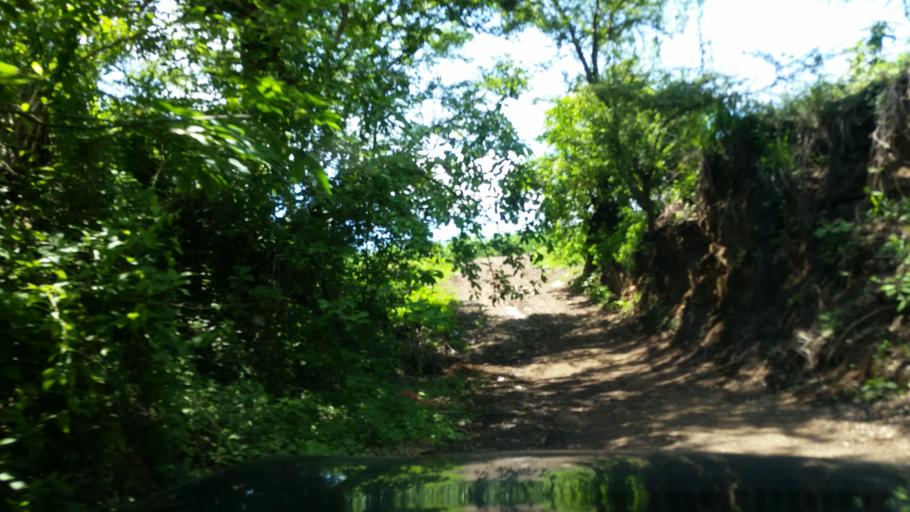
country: NI
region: Chinandega
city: Puerto Morazan
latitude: 12.7629
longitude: -87.1220
